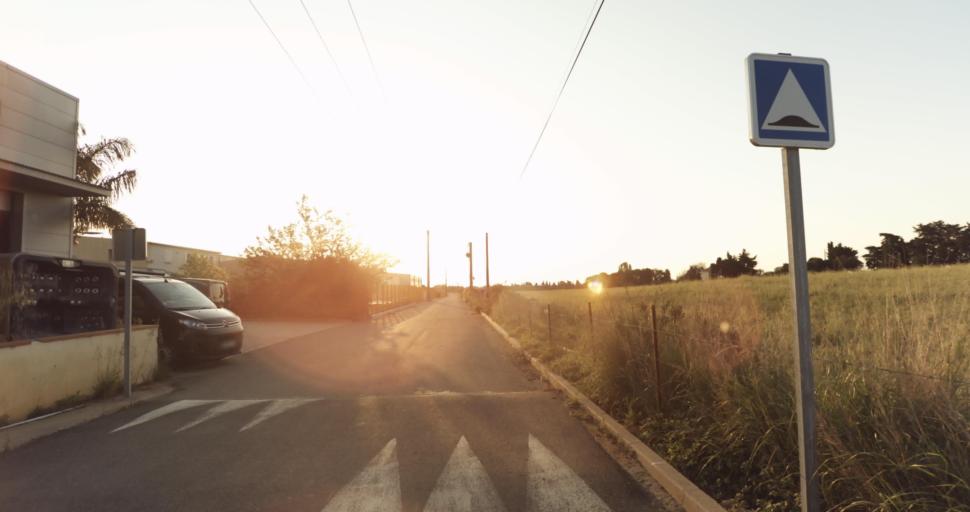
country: FR
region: Corsica
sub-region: Departement de la Haute-Corse
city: Biguglia
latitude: 42.5989
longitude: 9.4477
